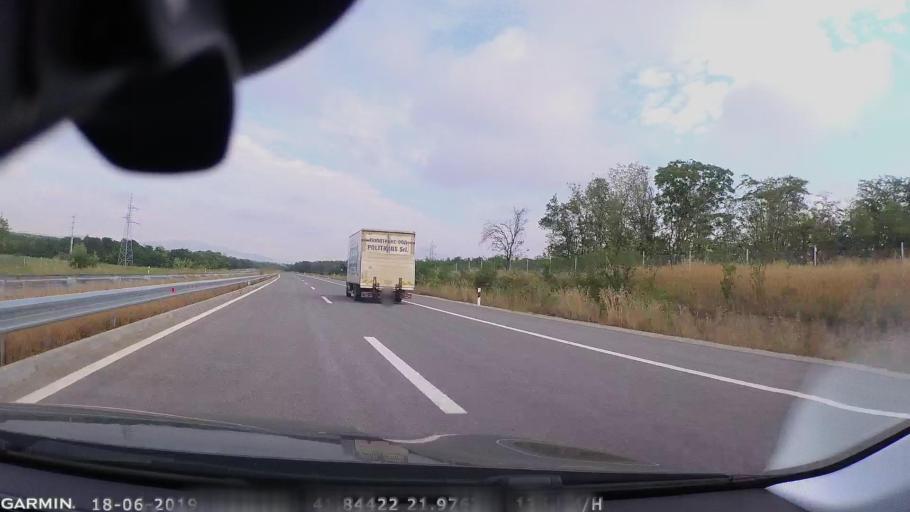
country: MK
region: Sveti Nikole
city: Sveti Nikole
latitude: 41.8449
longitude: 21.9756
